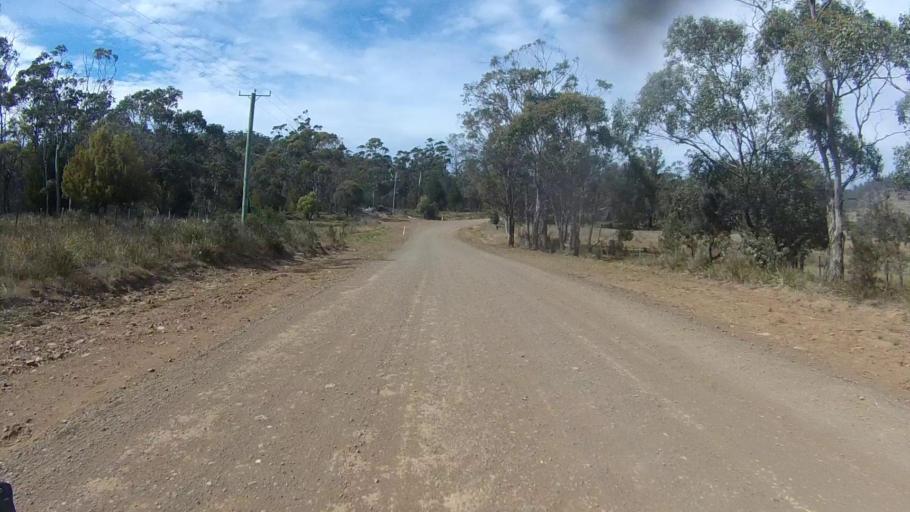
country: AU
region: Tasmania
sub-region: Sorell
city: Sorell
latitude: -42.6474
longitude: 147.8995
